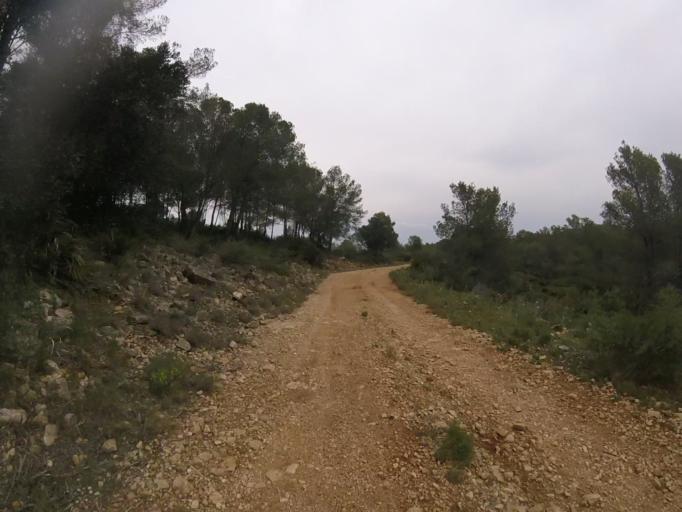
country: ES
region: Valencia
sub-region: Provincia de Castello
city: Alcala de Xivert
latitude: 40.3152
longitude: 0.2684
